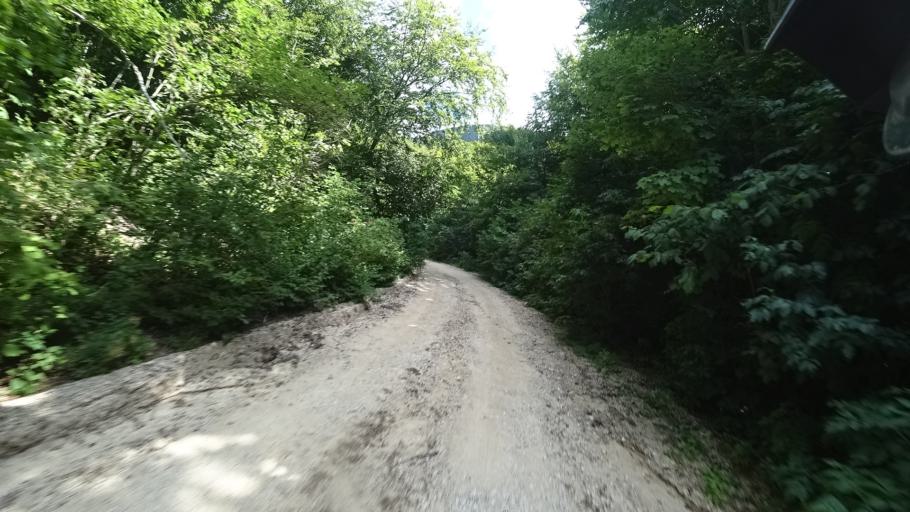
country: BA
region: Federation of Bosnia and Herzegovina
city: Orasac
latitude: 44.5703
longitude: 15.8474
